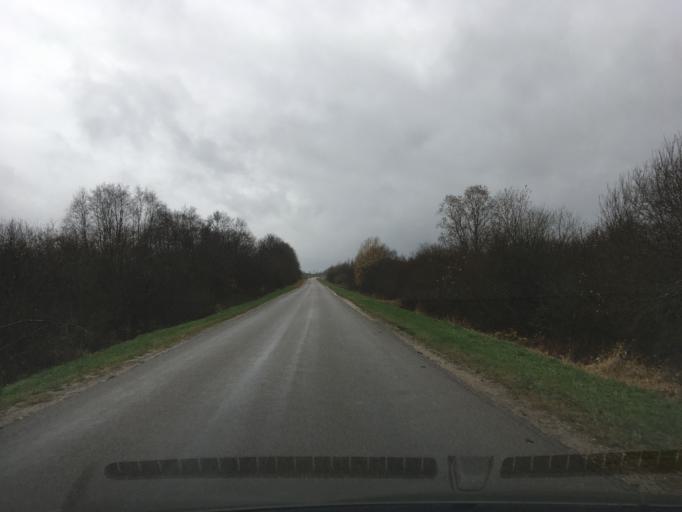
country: EE
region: Laeaene
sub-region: Lihula vald
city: Lihula
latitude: 58.7002
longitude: 23.8565
